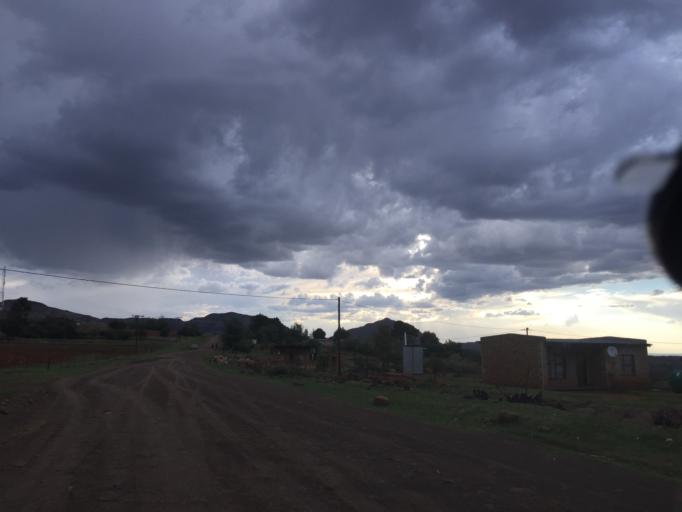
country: LS
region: Leribe
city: Leribe
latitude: -29.1525
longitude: 28.0401
